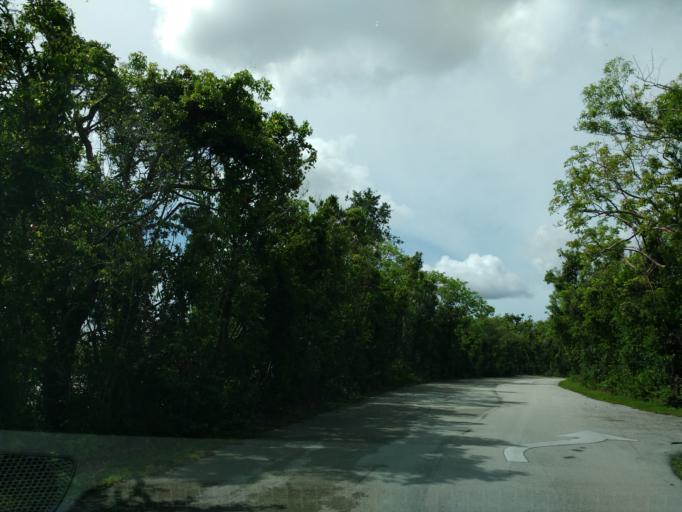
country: US
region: Florida
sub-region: Miami-Dade County
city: Florida City
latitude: 25.3836
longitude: -80.6105
